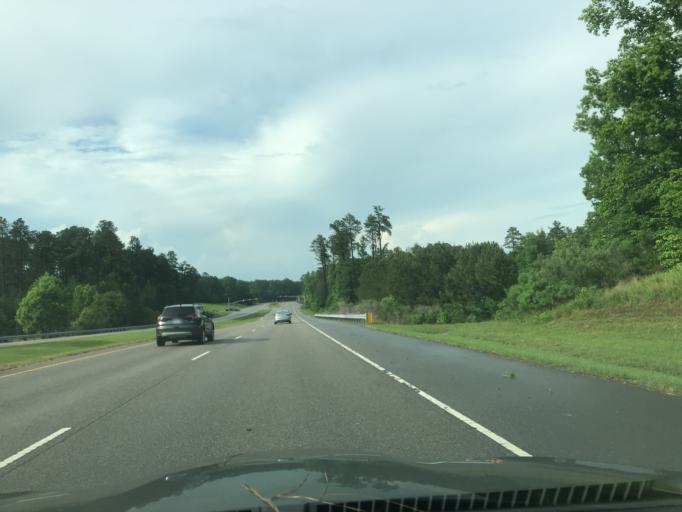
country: US
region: North Carolina
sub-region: Wake County
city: Morrisville
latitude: 35.8632
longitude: -78.8726
